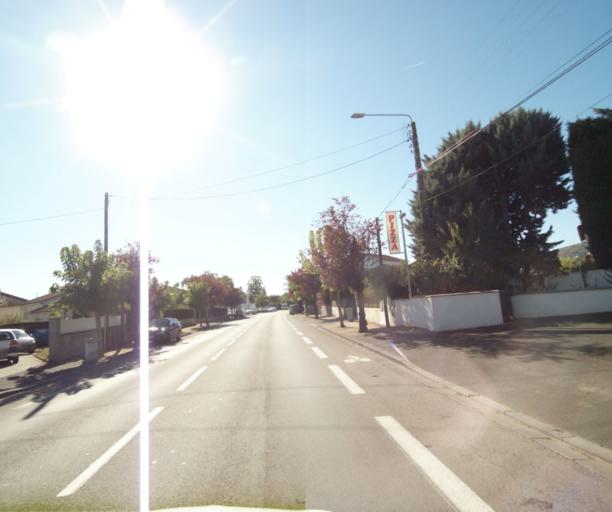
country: FR
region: Auvergne
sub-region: Departement du Puy-de-Dome
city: Cebazat
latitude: 45.8230
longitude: 3.1062
